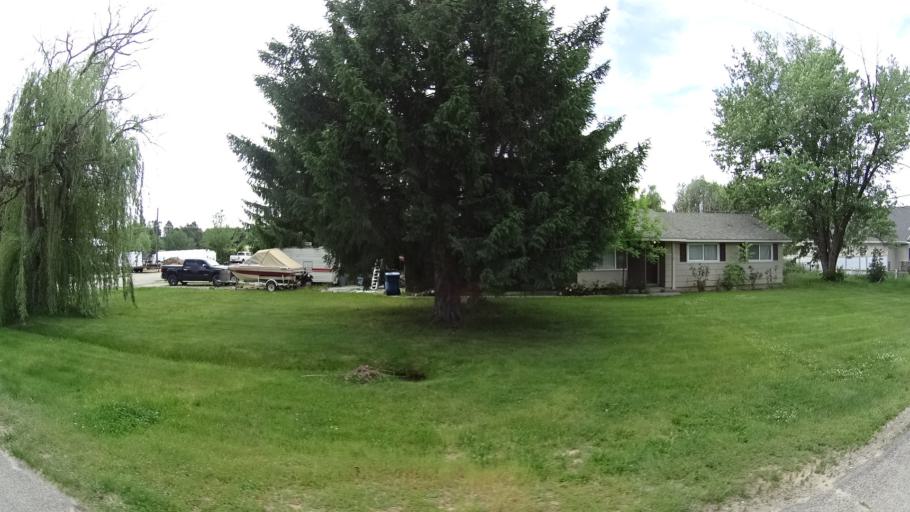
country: US
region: Idaho
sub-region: Ada County
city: Eagle
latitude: 43.6448
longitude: -116.3285
